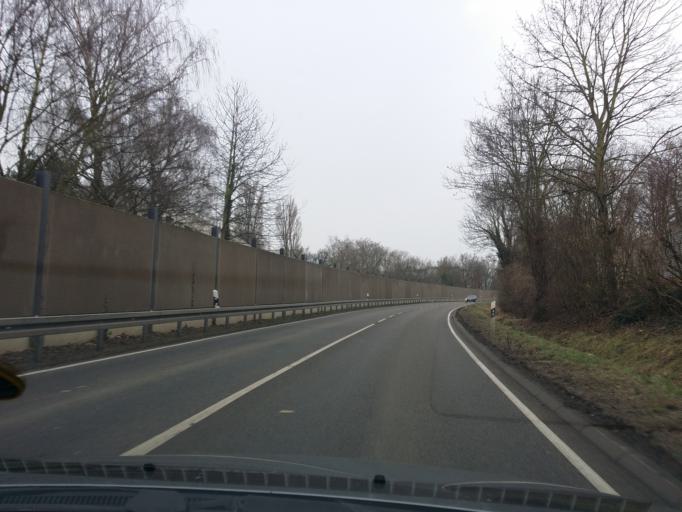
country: DE
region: Hesse
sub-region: Regierungsbezirk Darmstadt
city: Hochheim am Main
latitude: 50.0445
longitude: 8.3585
